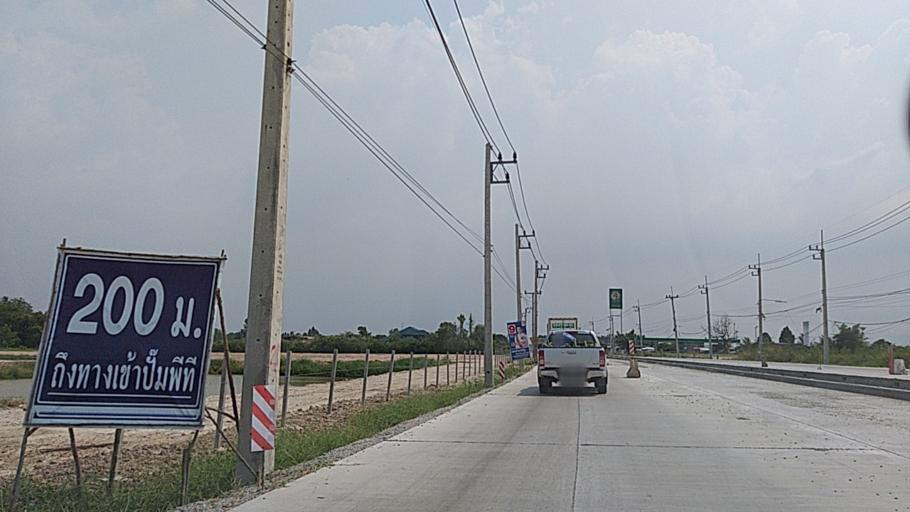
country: TH
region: Chon Buri
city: Phanat Nikhom
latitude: 13.3830
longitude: 101.1935
